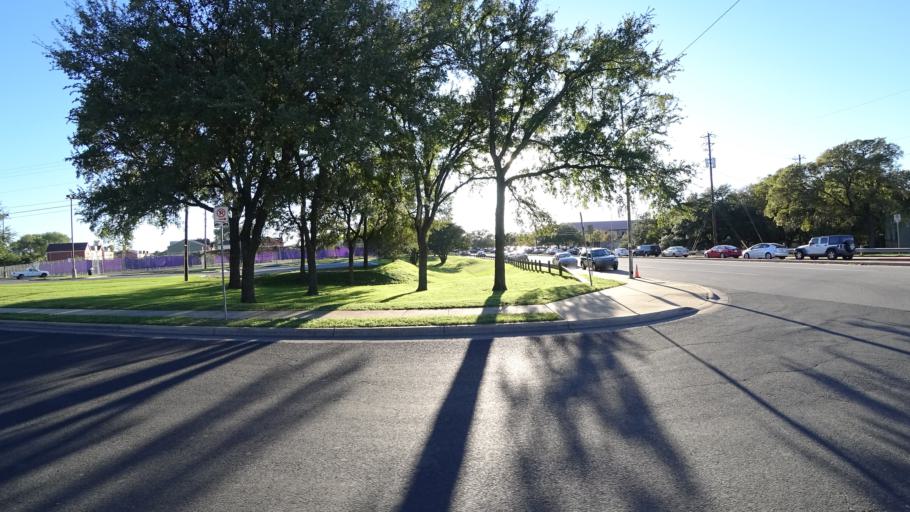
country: US
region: Texas
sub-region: Travis County
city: Austin
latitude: 30.2371
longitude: -97.7021
